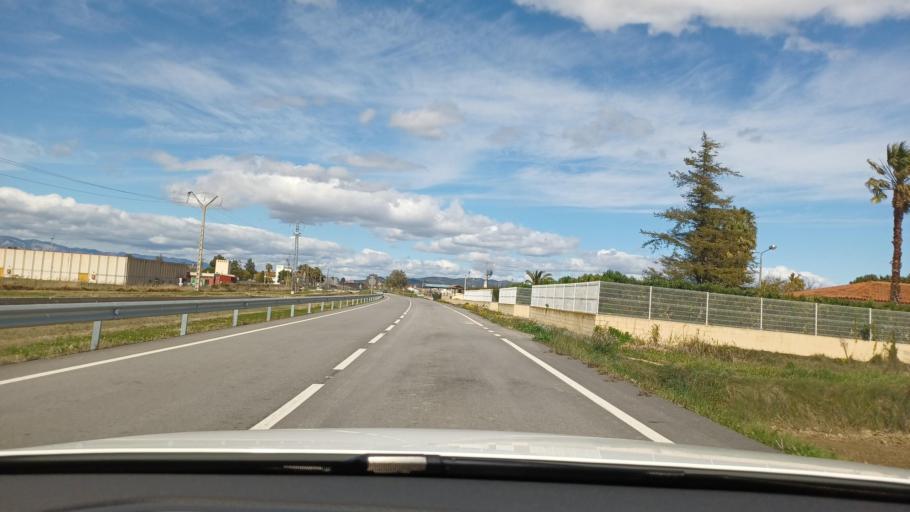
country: ES
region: Catalonia
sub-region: Provincia de Tarragona
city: Amposta
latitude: 40.7002
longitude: 0.5886
